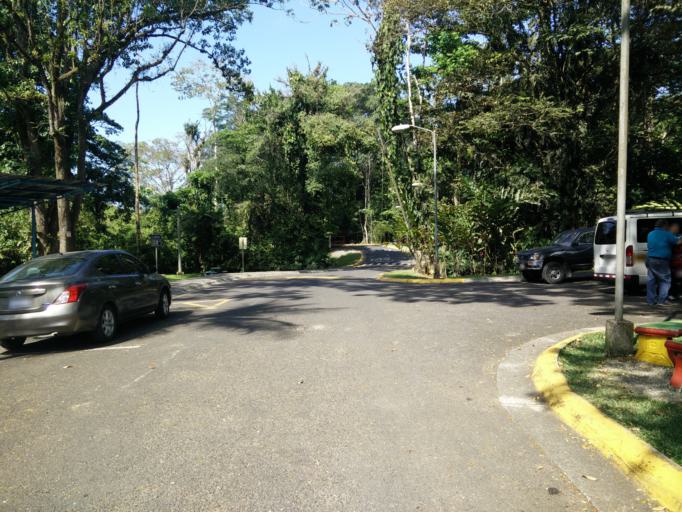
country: CR
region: Limon
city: Limon
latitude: 9.9833
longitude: -83.0625
